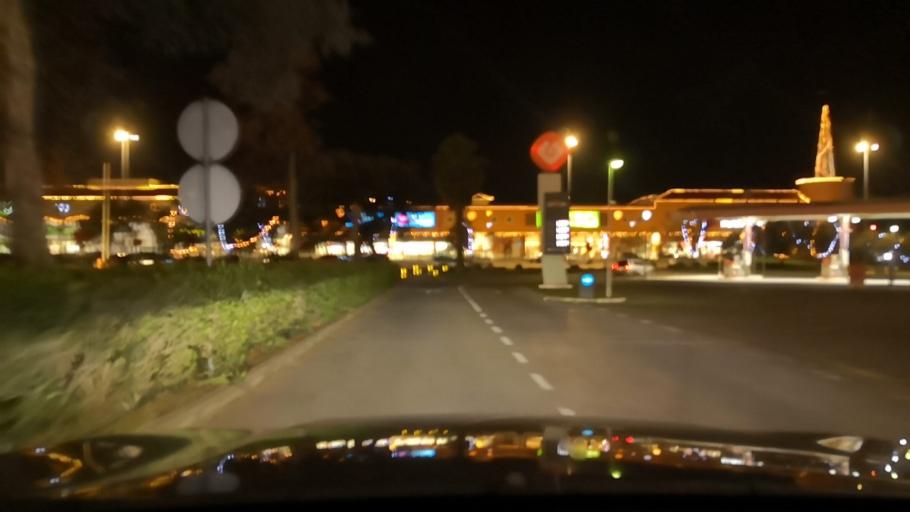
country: PT
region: Setubal
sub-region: Montijo
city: Montijo
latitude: 38.6971
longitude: -8.9424
